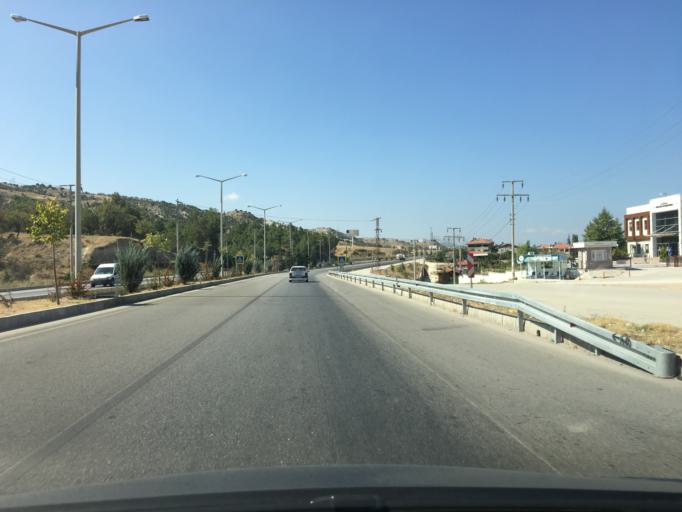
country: TR
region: Burdur
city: Burdur
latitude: 37.7531
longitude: 30.3337
